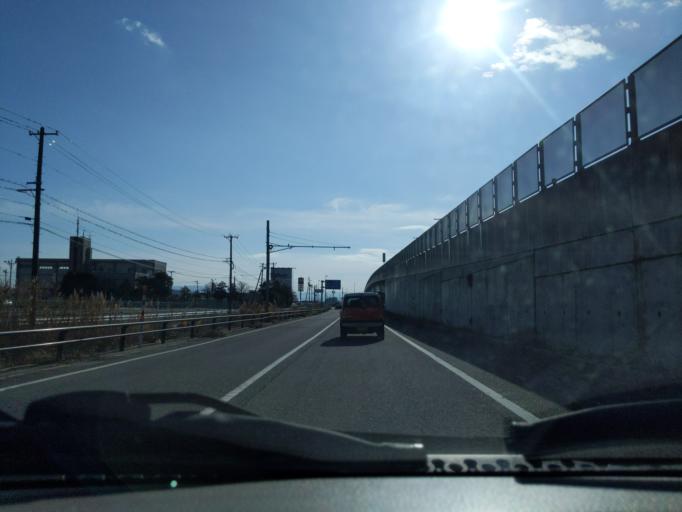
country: JP
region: Niigata
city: Kameda-honcho
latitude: 37.8714
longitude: 139.0870
